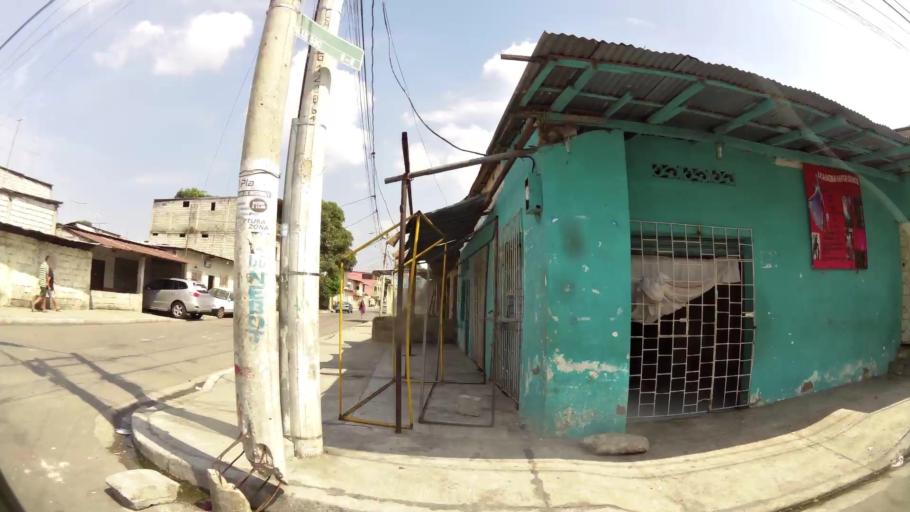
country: EC
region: Guayas
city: Guayaquil
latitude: -2.2628
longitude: -79.8841
